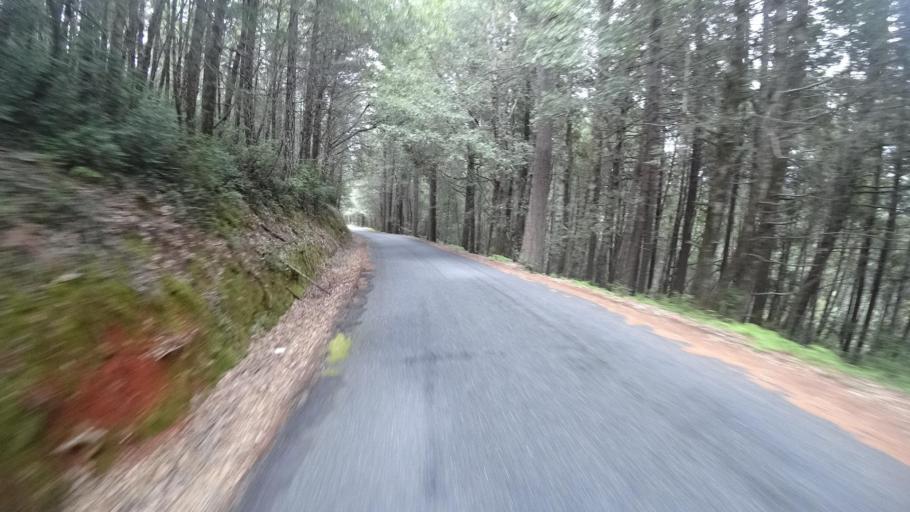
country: US
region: California
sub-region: Humboldt County
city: Willow Creek
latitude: 41.1981
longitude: -123.7683
